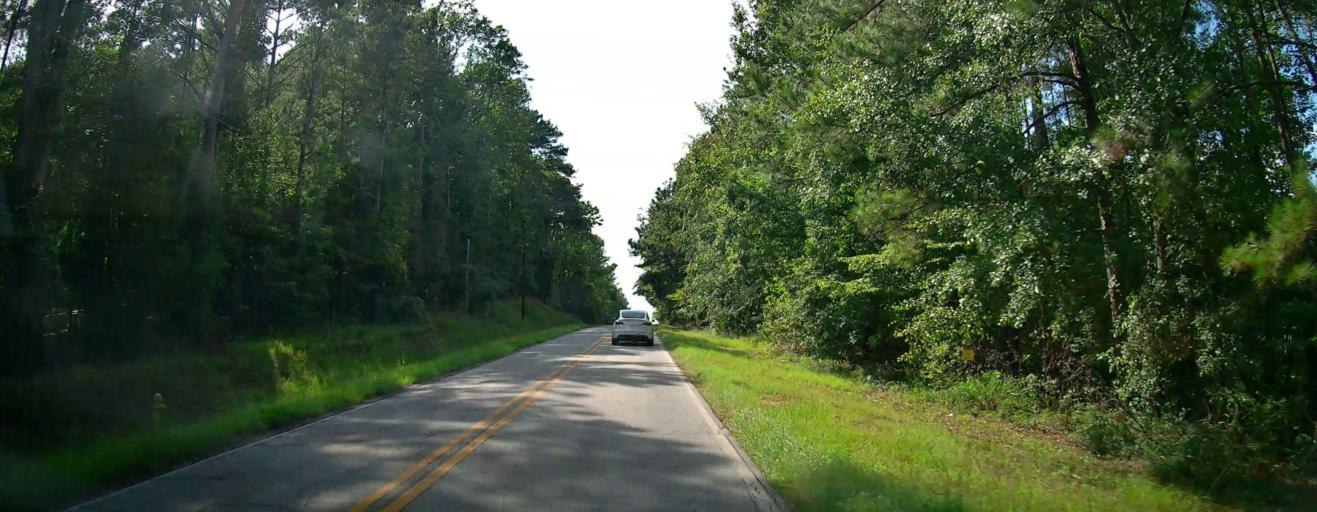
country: US
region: Alabama
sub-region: Russell County
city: Phenix City
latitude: 32.5896
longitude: -84.9212
